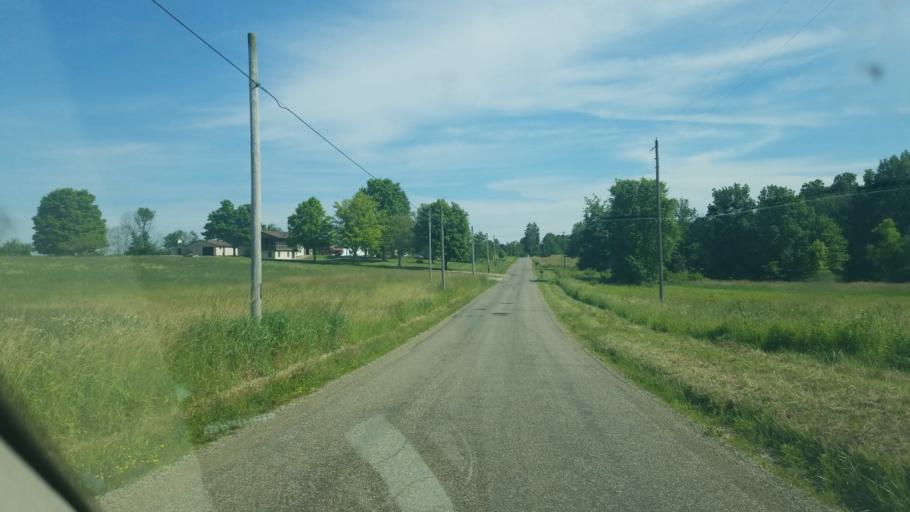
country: US
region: Ohio
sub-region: Holmes County
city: Millersburg
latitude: 40.4862
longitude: -81.9656
